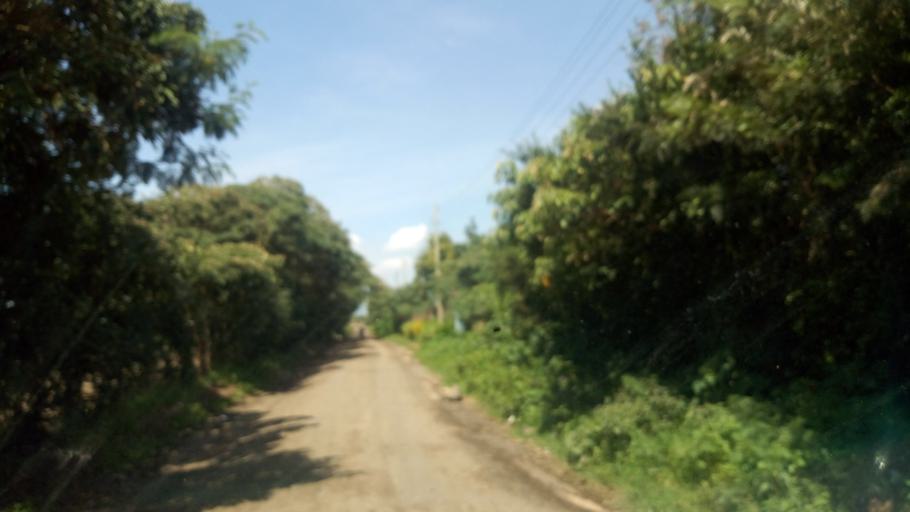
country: KE
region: Nakuru
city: Nakuru
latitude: -0.2770
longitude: 36.1144
